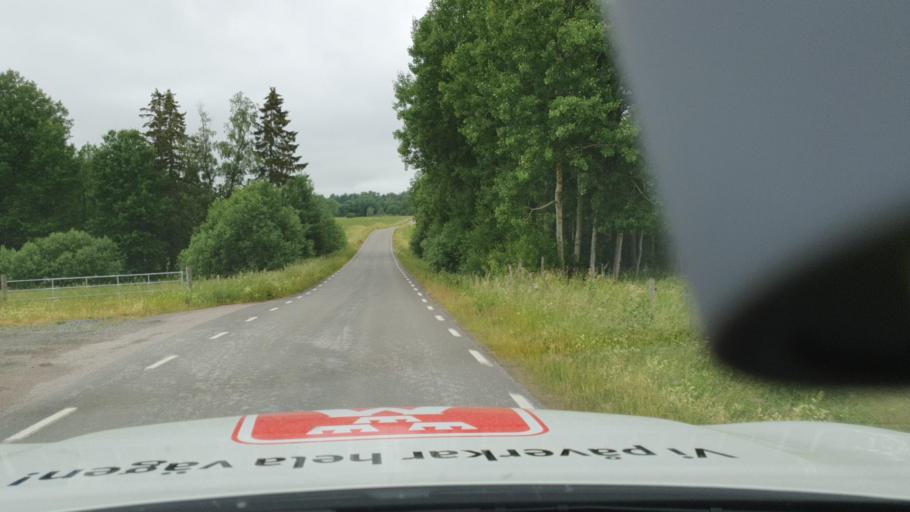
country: SE
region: Vaestra Goetaland
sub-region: Tidaholms Kommun
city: Olofstorp
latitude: 58.3924
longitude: 13.9897
